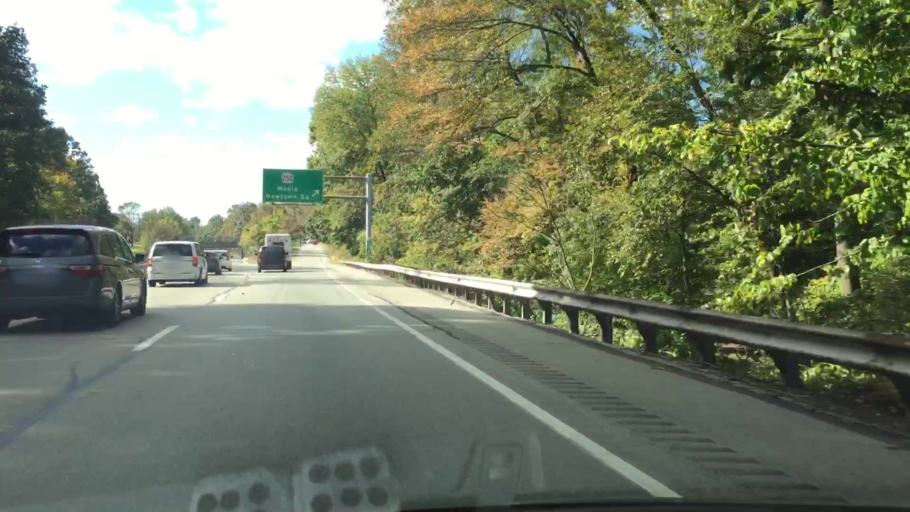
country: US
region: Pennsylvania
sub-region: Delaware County
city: Media
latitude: 39.9367
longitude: -75.3870
